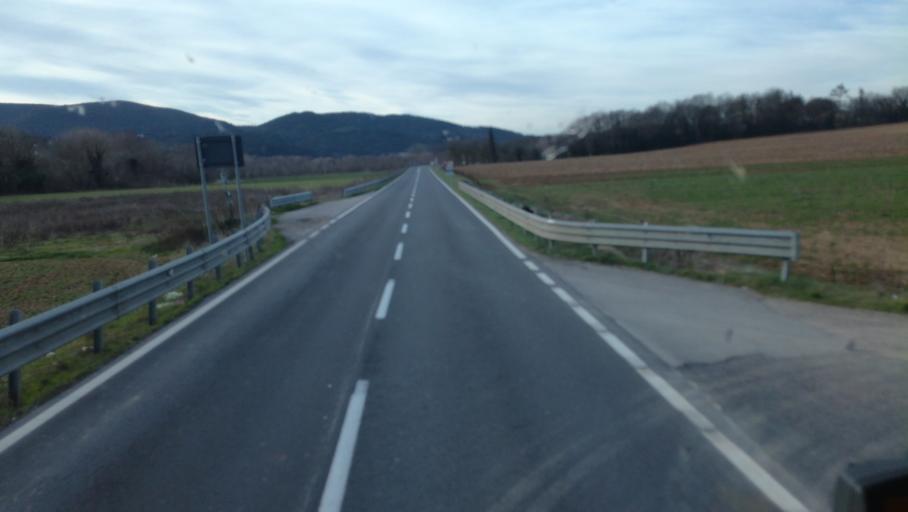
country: IT
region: Tuscany
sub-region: Provincia di Siena
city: Rosia
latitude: 43.1695
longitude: 11.2837
